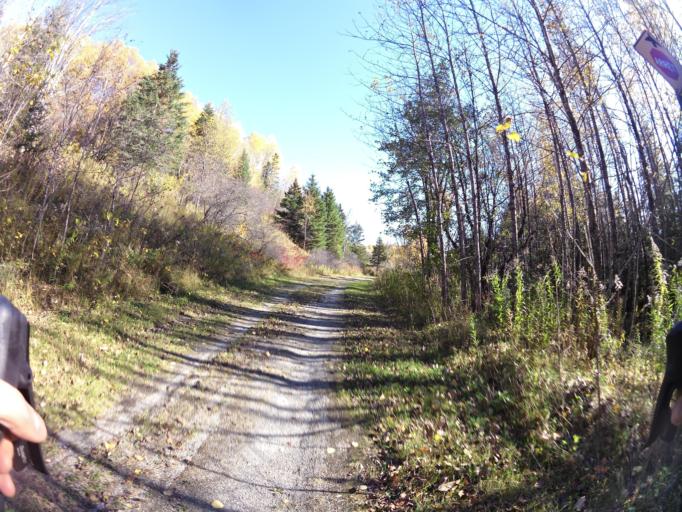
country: CA
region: Quebec
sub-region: Outaouais
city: Wakefield
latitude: 45.8450
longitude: -75.9813
